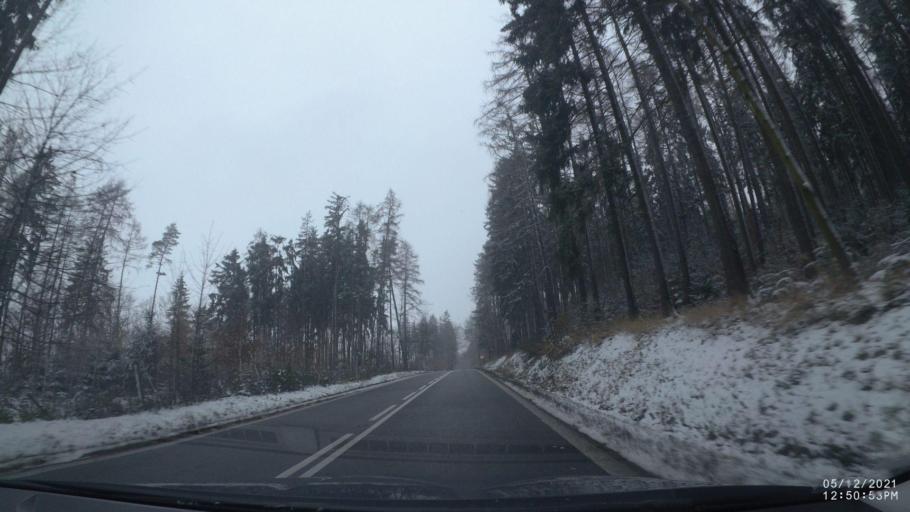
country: CZ
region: Kralovehradecky
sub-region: Okres Nachod
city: Nachod
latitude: 50.3909
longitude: 16.1407
